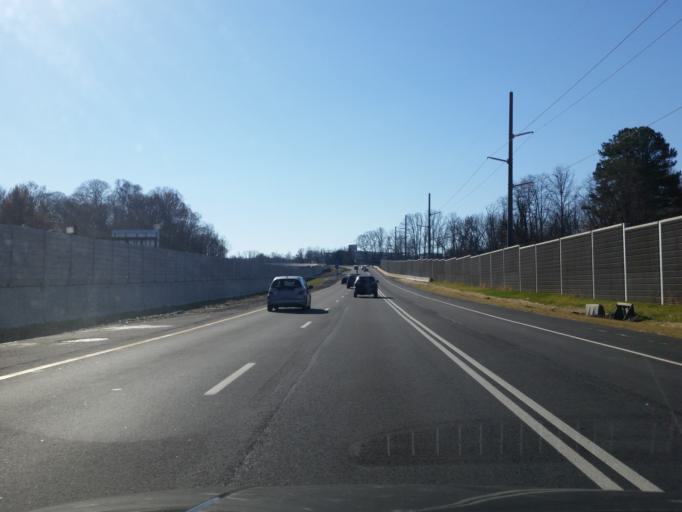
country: US
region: Virginia
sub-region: Fairfax County
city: Pimmit Hills
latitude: 38.9080
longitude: -77.1874
